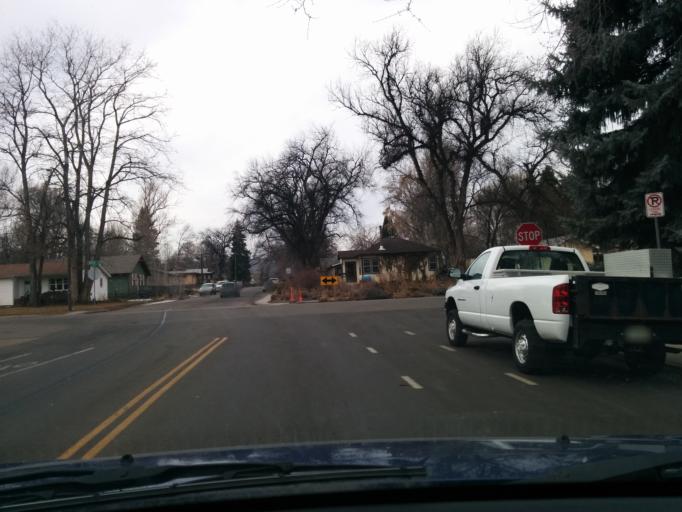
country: US
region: Colorado
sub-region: Larimer County
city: Fort Collins
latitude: 40.5922
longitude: -105.0907
